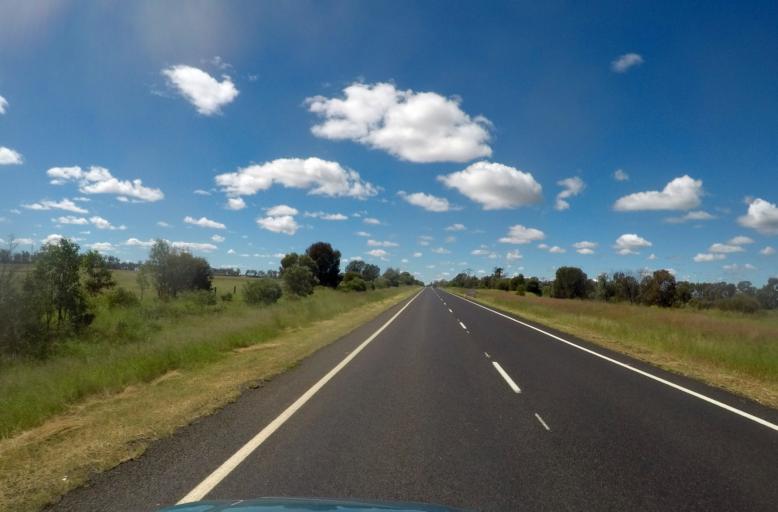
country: AU
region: Queensland
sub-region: Western Downs
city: Westcourt
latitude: -26.6418
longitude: 149.9918
